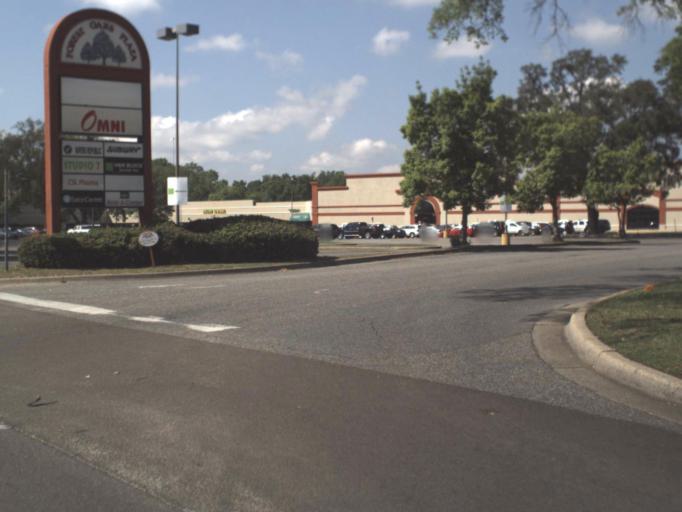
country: US
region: Florida
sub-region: Escambia County
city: Brent
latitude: 30.4715
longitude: -87.2251
